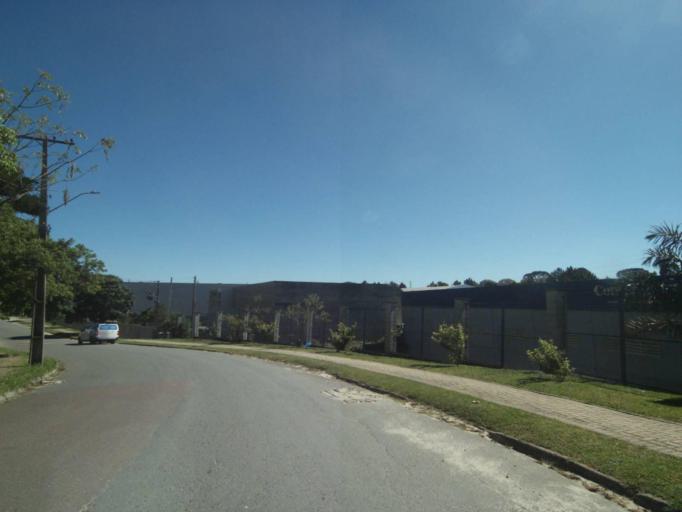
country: BR
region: Parana
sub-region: Curitiba
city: Curitiba
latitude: -25.4889
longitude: -49.3431
